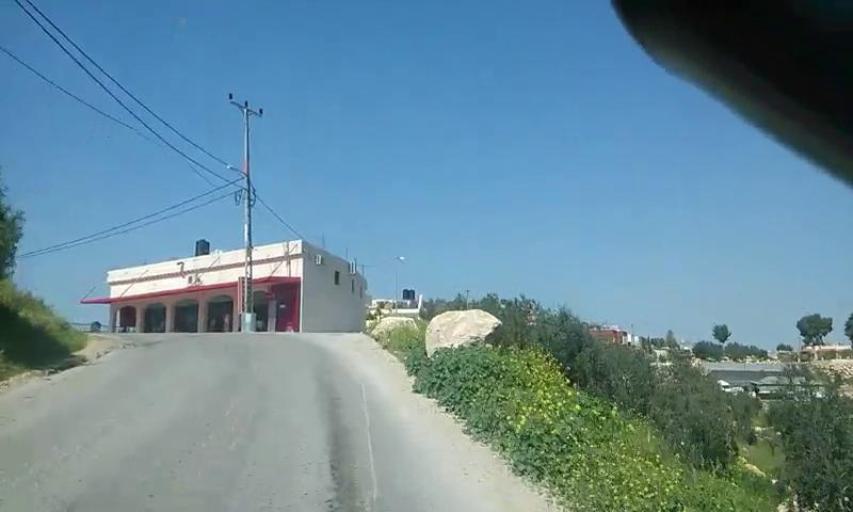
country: PS
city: Dayr Samit
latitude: 31.5279
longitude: 34.9777
